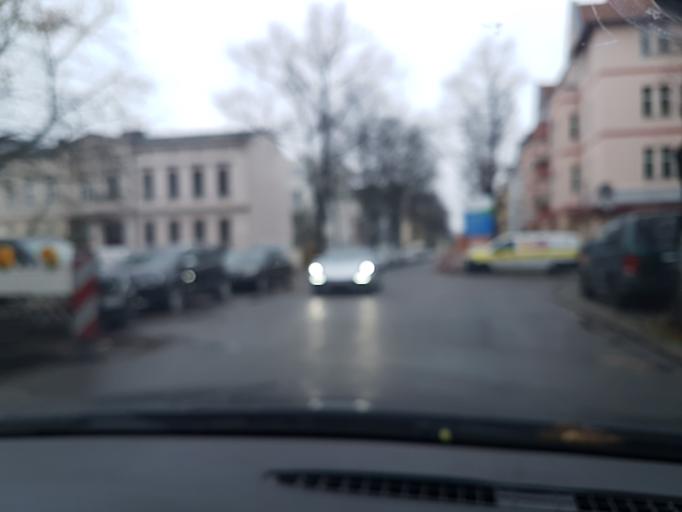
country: DE
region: Berlin
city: Tempelhof Bezirk
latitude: 52.4671
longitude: 13.3832
